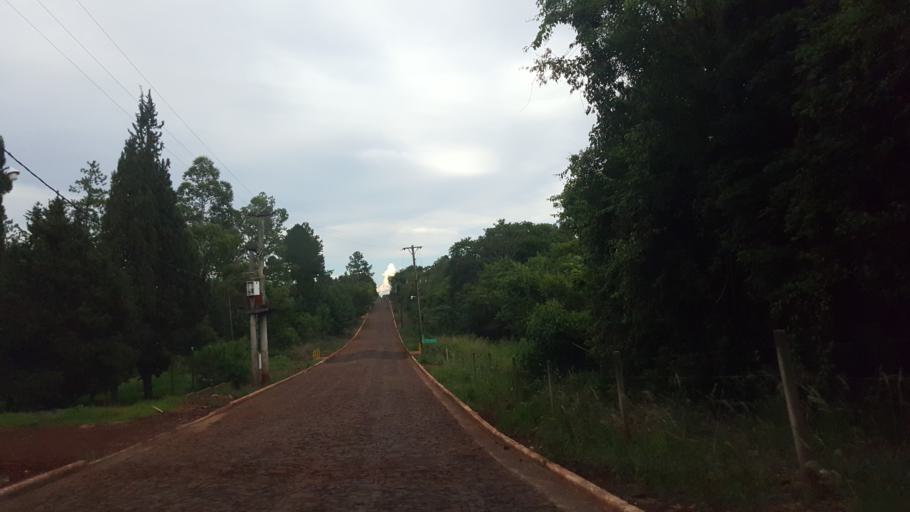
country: AR
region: Misiones
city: Jardin America
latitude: -27.0817
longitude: -55.2864
